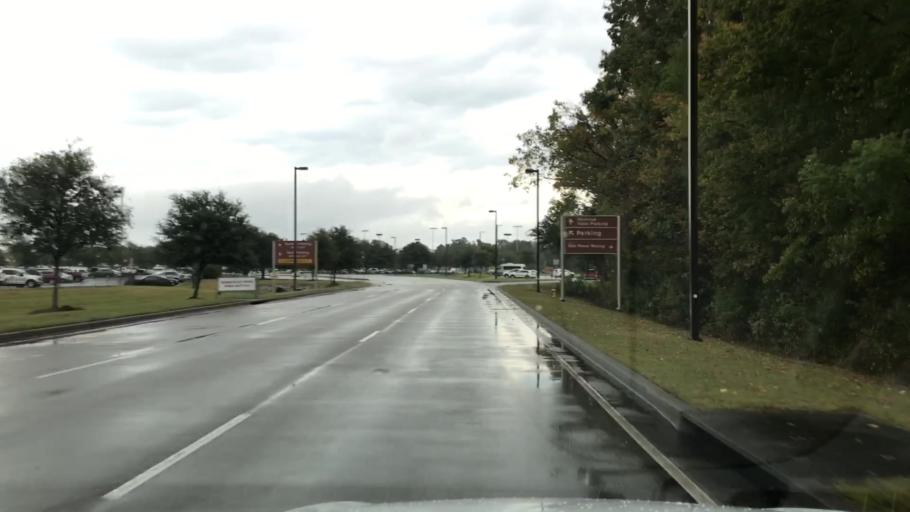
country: US
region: South Carolina
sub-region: Berkeley County
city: Hanahan
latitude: 32.8802
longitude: -80.0352
